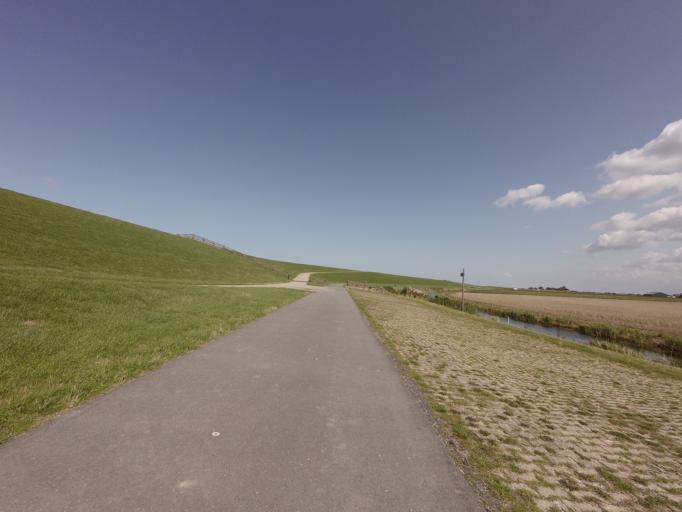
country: NL
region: Friesland
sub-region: Gemeente Dongeradeel
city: Holwerd
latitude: 53.3760
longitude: 5.8781
